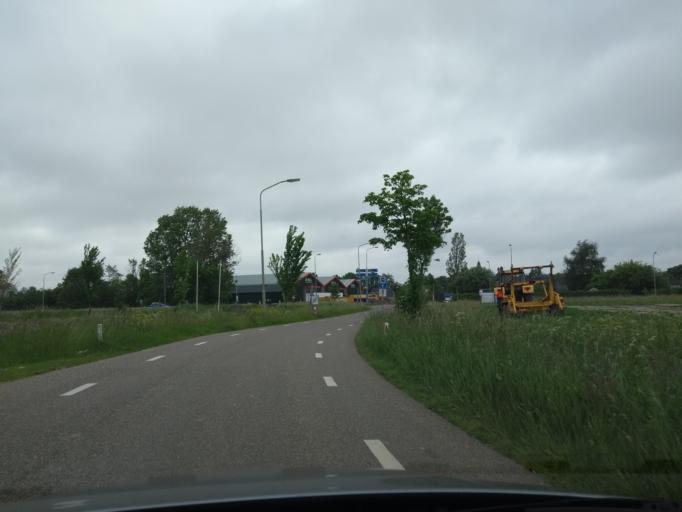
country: NL
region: Groningen
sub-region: Gemeente Zuidhorn
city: Oldehove
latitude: 53.3545
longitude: 6.4253
